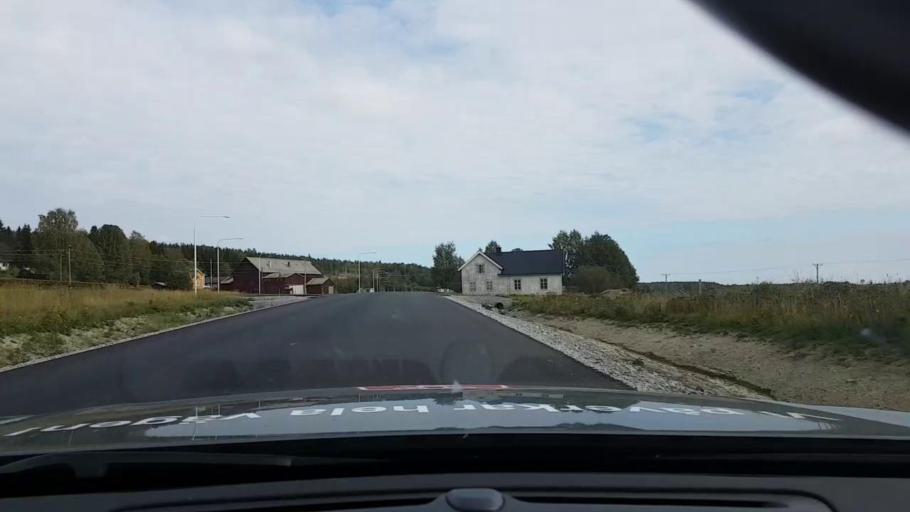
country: SE
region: Vaesternorrland
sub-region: OErnskoeldsviks Kommun
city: Bjasta
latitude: 63.2914
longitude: 18.4641
